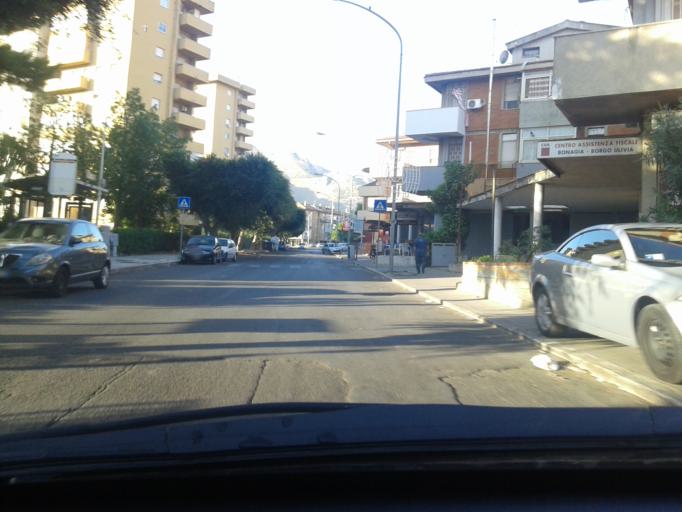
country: IT
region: Sicily
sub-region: Palermo
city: Palermo
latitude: 38.0921
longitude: 13.3603
